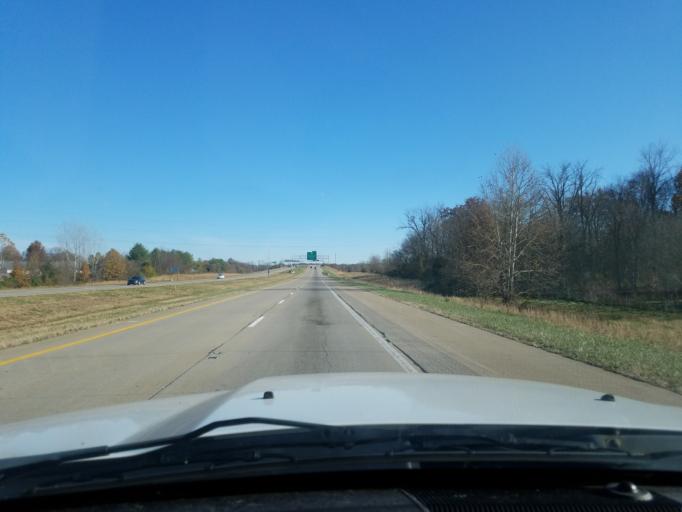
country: US
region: Indiana
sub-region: Clark County
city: Oak Park
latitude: 38.3475
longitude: -85.7263
